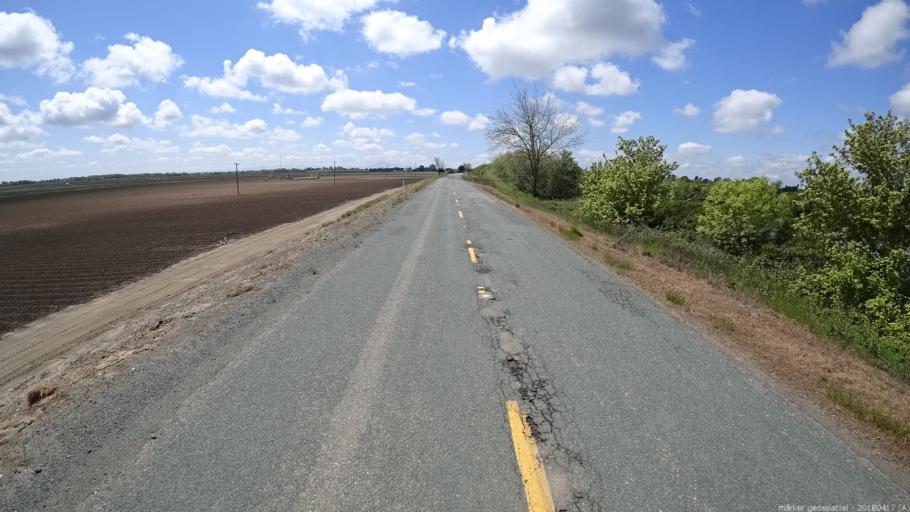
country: US
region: California
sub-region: Sacramento County
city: Walnut Grove
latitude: 38.1835
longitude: -121.5670
